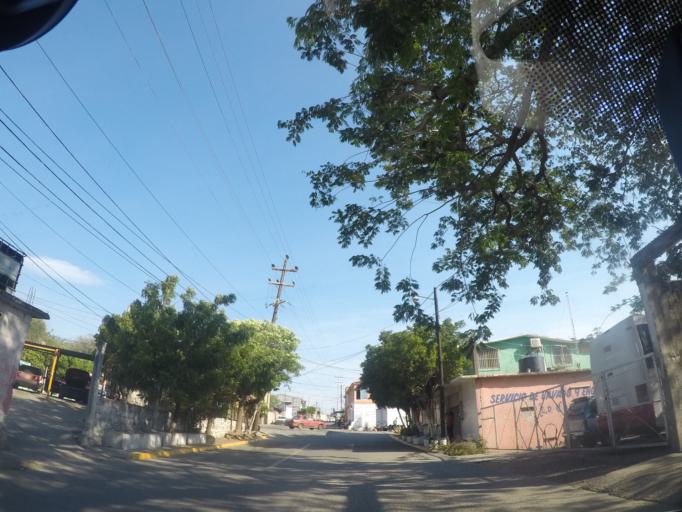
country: MX
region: Oaxaca
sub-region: Salina Cruz
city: Salina Cruz
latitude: 16.1964
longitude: -95.2025
